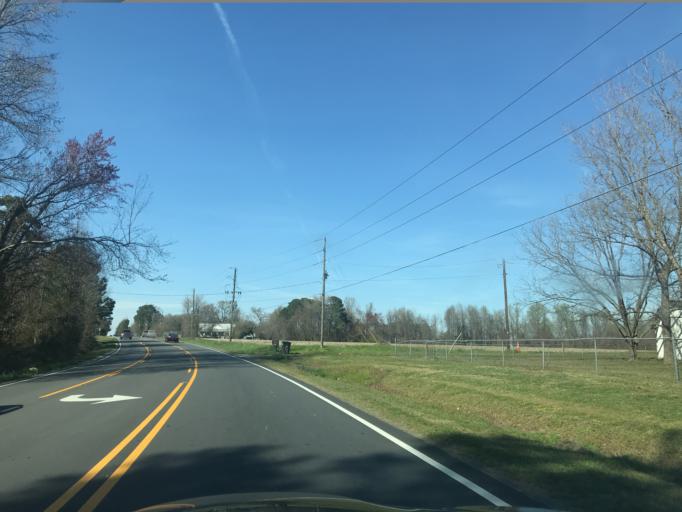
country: US
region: North Carolina
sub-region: Wake County
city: Fuquay-Varina
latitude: 35.5578
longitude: -78.7544
